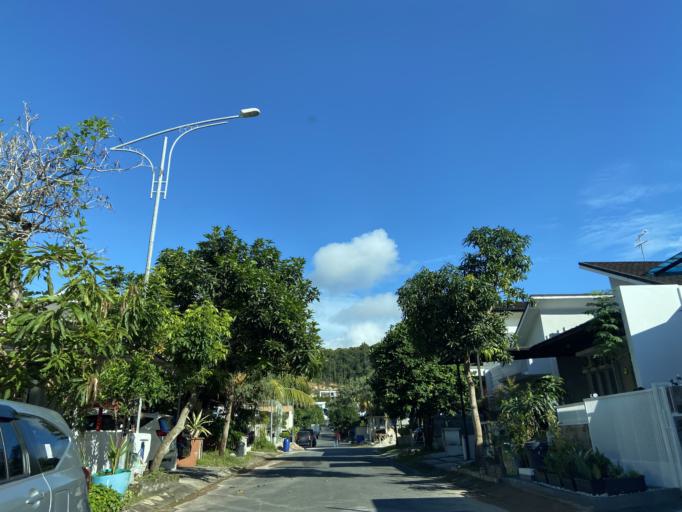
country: SG
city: Singapore
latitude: 1.0909
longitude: 104.0301
